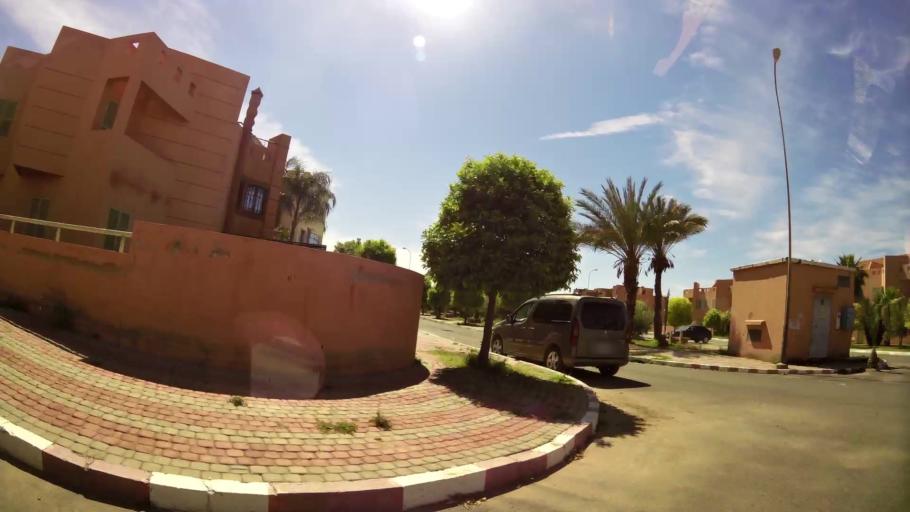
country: MA
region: Marrakech-Tensift-Al Haouz
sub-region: Marrakech
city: Marrakesh
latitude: 31.6373
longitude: -8.1068
